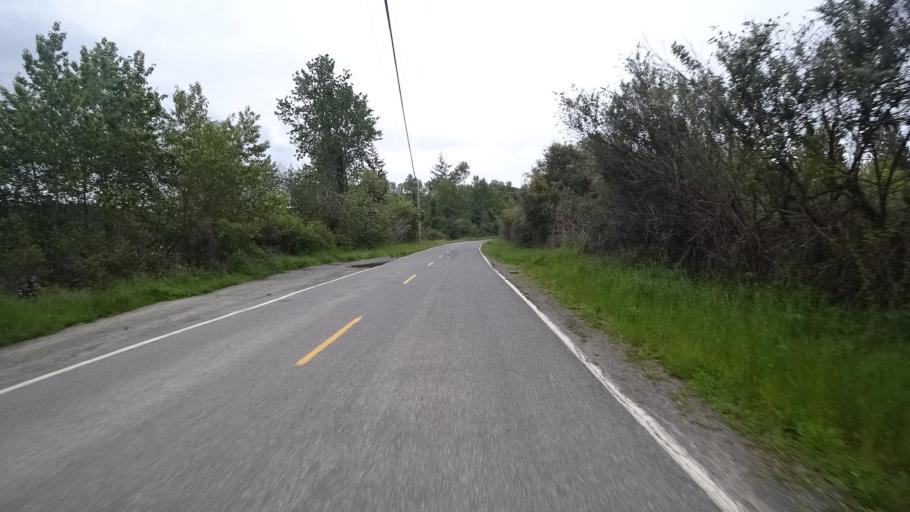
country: US
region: California
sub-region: Humboldt County
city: Blue Lake
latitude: 40.8705
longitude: -123.9942
